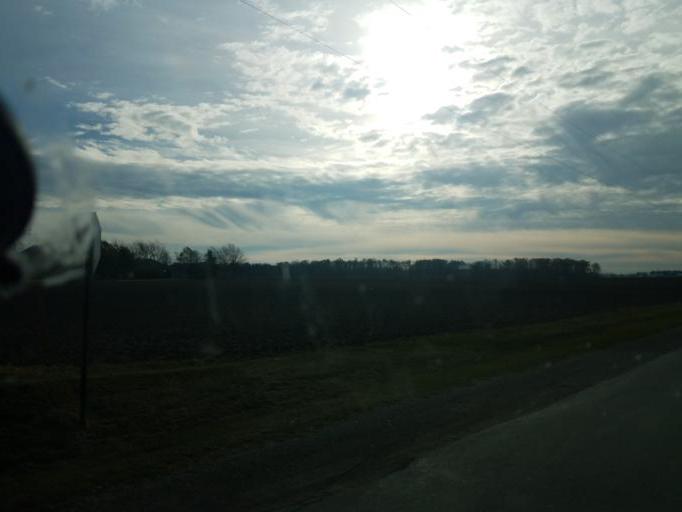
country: US
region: Ohio
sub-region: Crawford County
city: Galion
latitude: 40.7193
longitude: -82.8993
